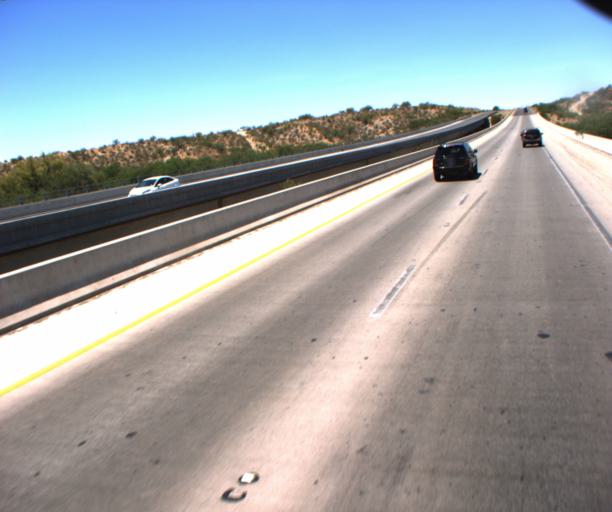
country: US
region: Arizona
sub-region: Pima County
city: Oro Valley
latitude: 32.4266
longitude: -110.9522
